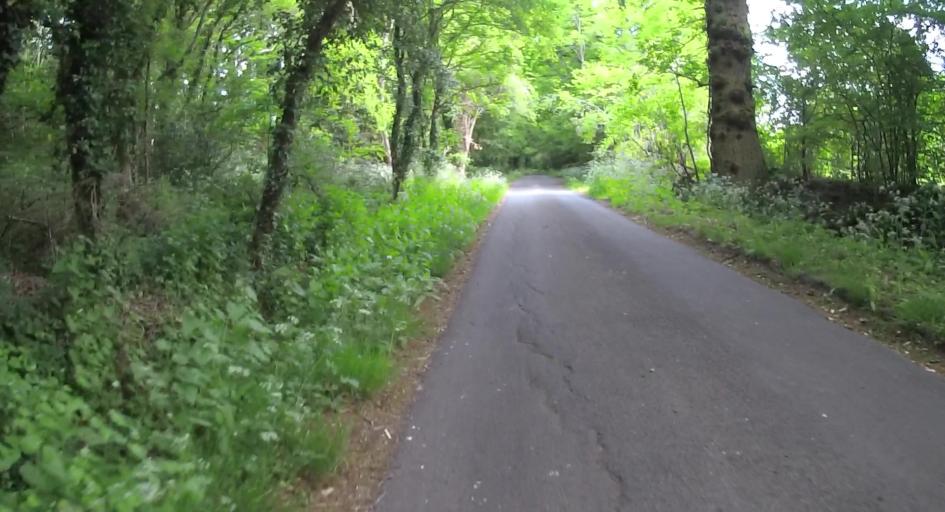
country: GB
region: England
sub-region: Hampshire
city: Fleet
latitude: 51.2362
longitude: -0.8541
